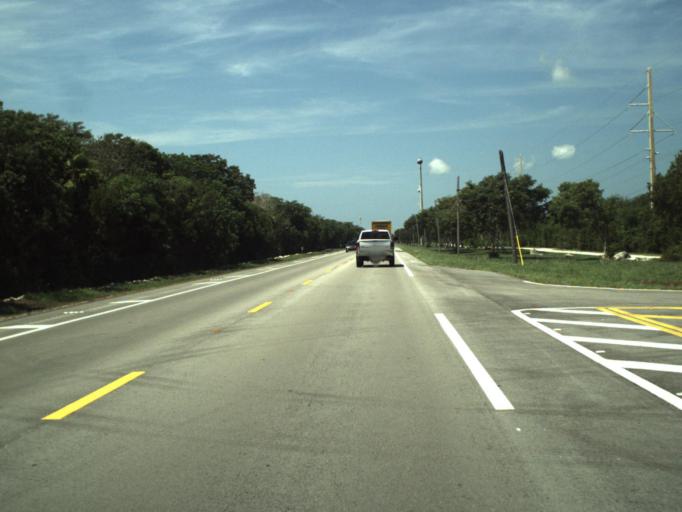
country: US
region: Florida
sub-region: Monroe County
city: Marathon
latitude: 24.7411
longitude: -80.9971
